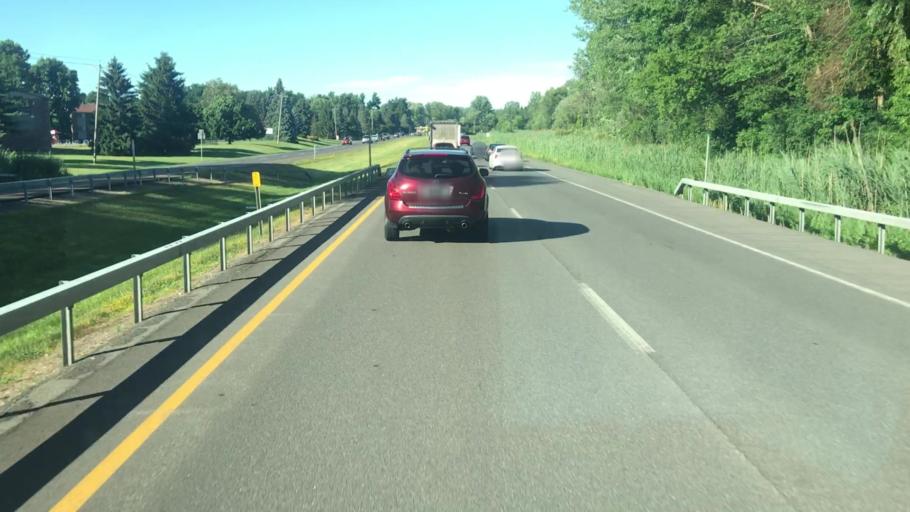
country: US
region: New York
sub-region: Onondaga County
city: Liverpool
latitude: 43.1263
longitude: -76.2439
